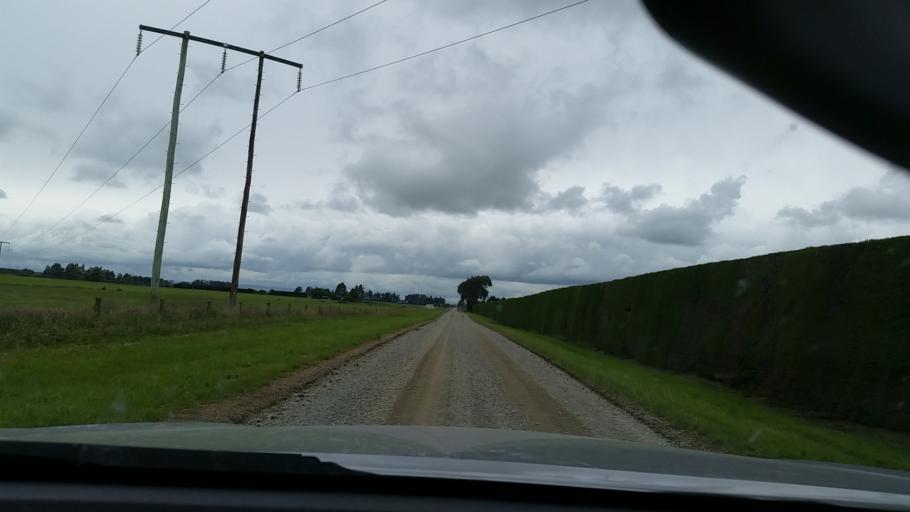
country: NZ
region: Southland
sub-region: Southland District
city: Winton
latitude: -46.2569
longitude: 168.3673
